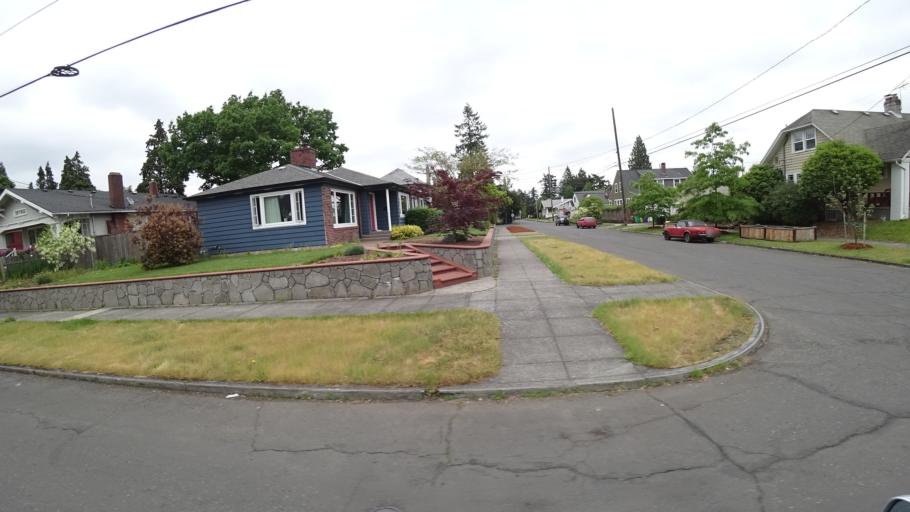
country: US
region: Oregon
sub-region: Multnomah County
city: Portland
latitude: 45.5455
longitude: -122.6056
